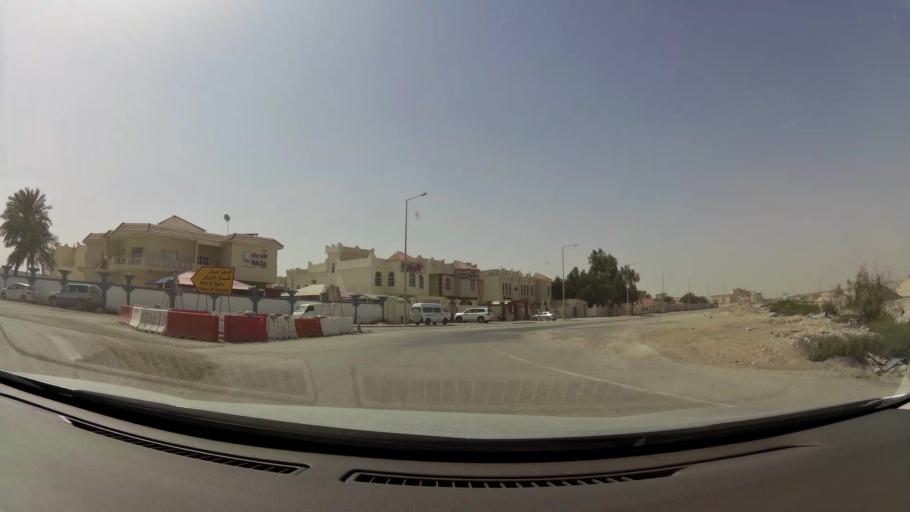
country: QA
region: Baladiyat Umm Salal
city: Umm Salal Muhammad
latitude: 25.3729
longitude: 51.4403
